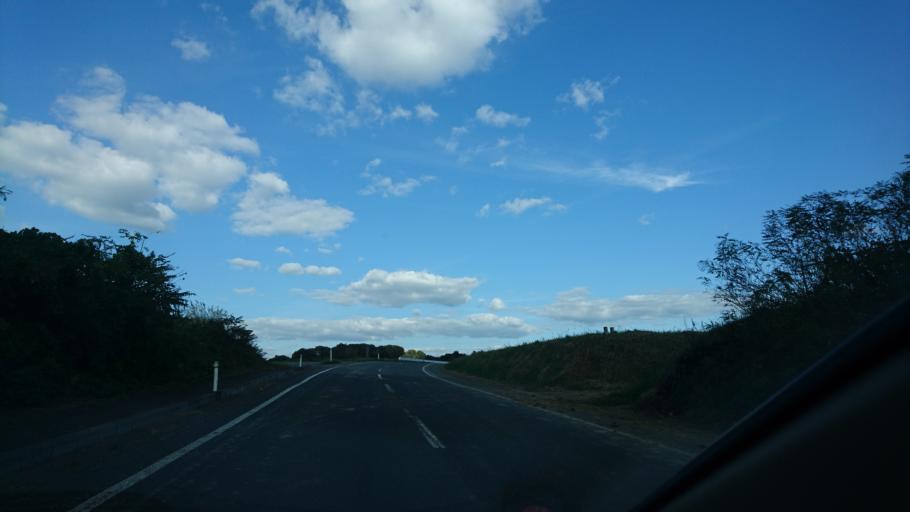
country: JP
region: Iwate
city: Kitakami
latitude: 39.2364
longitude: 141.1294
